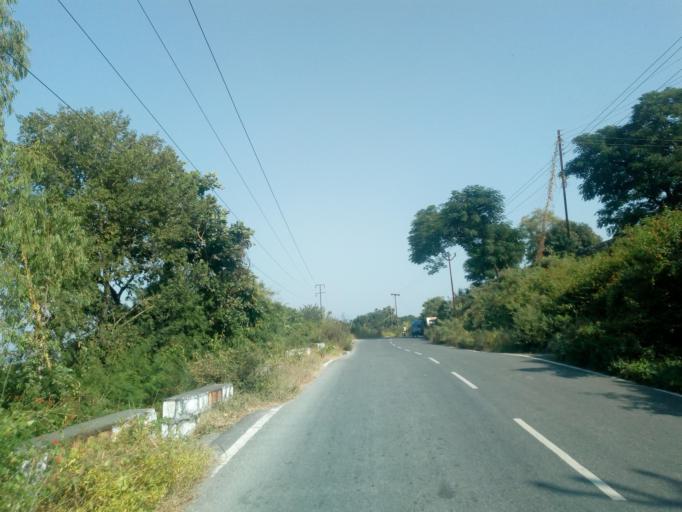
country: IN
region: Uttarakhand
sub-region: Dehradun
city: Harbatpur
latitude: 30.4416
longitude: 77.6869
